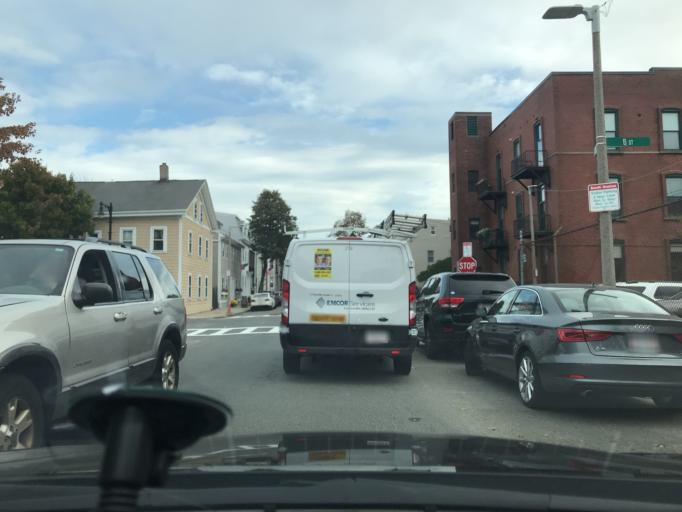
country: US
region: Massachusetts
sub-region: Suffolk County
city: South Boston
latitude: 42.3418
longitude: -71.0533
